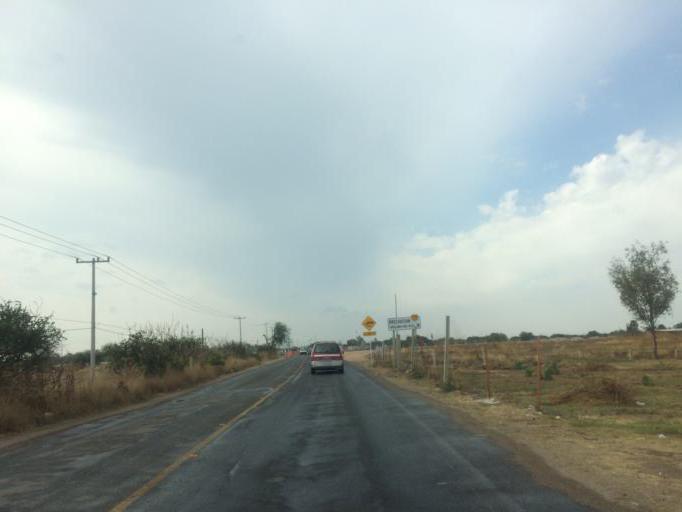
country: MX
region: Guanajuato
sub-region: Leon
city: Ladrilleras del Refugio
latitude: 21.0799
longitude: -101.5445
